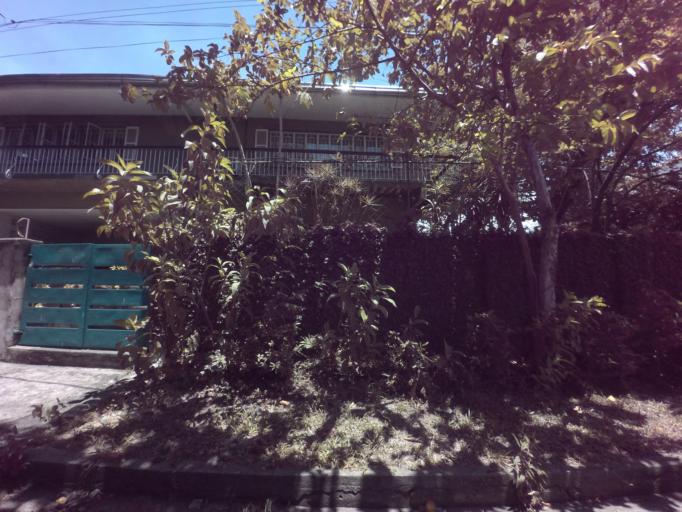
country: PH
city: Sambayanihan People's Village
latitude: 14.4865
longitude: 121.0391
